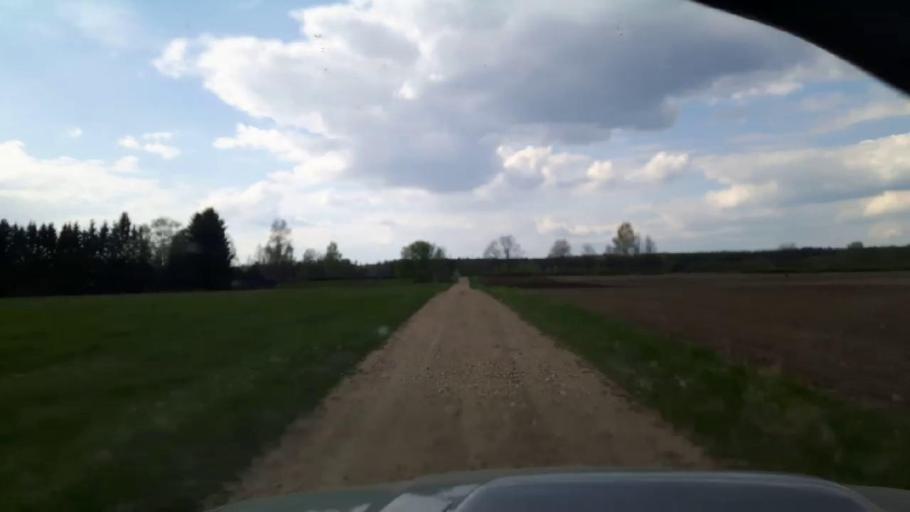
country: EE
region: Paernumaa
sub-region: Sindi linn
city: Sindi
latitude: 58.4384
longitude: 24.7440
